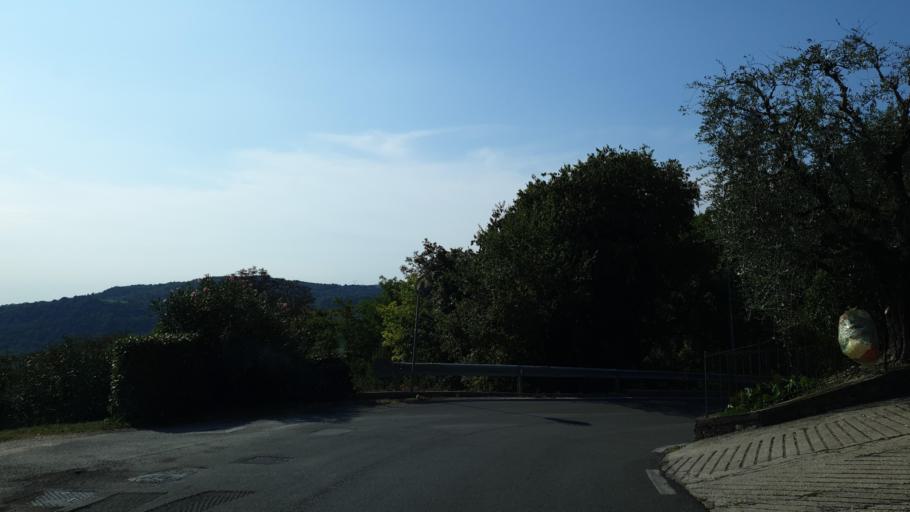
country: IT
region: Lombardy
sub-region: Provincia di Brescia
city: Roe Volciano
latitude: 45.6173
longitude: 10.4778
